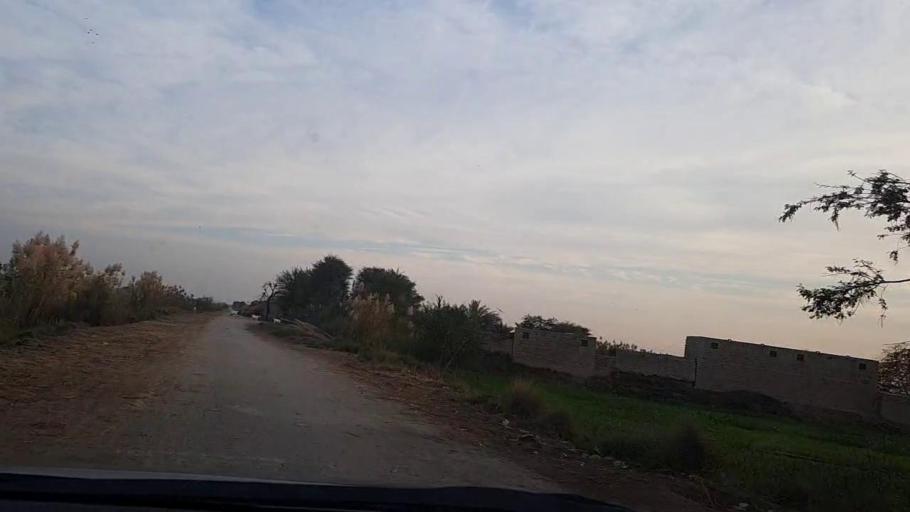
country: PK
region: Sindh
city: Sakrand
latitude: 26.1836
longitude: 68.3396
